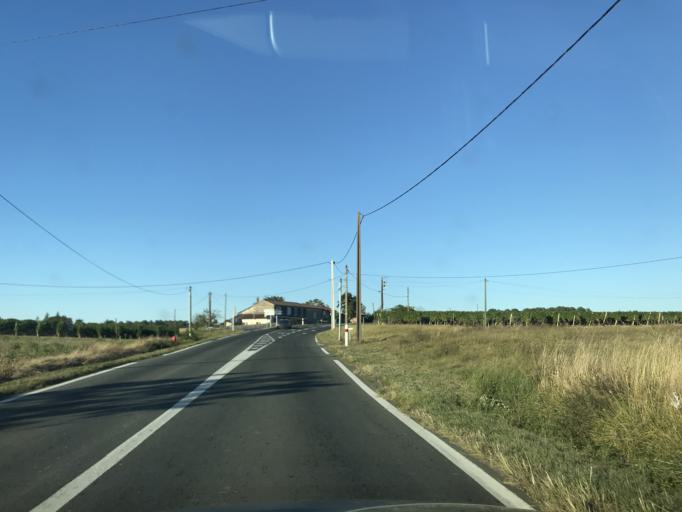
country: FR
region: Aquitaine
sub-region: Departement de la Gironde
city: Sauveterre-de-Guyenne
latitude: 44.7051
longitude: -0.0683
